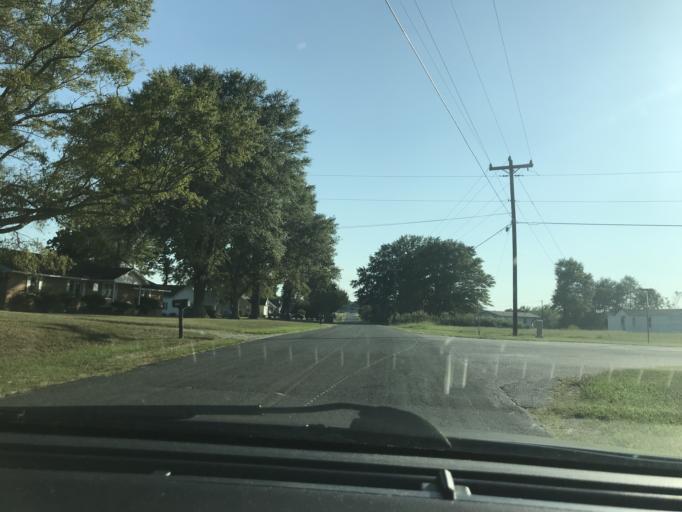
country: US
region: North Carolina
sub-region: Cleveland County
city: Boiling Springs
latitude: 35.1722
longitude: -81.7282
